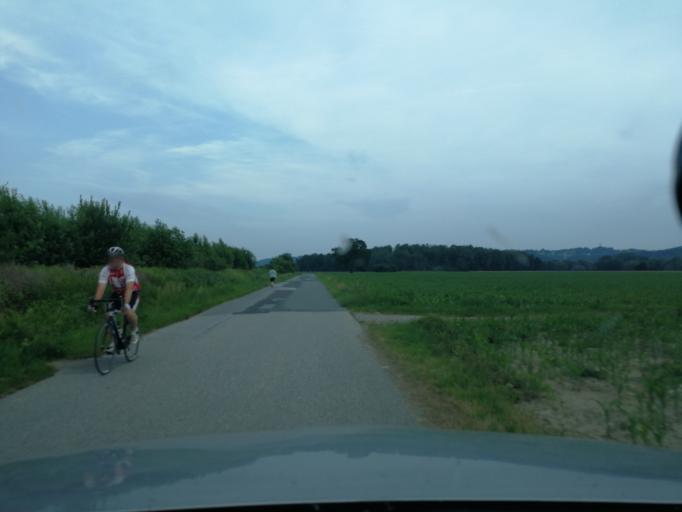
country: AT
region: Burgenland
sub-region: Politischer Bezirk Jennersdorf
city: Konigsdorf
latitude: 47.0127
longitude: 16.1546
